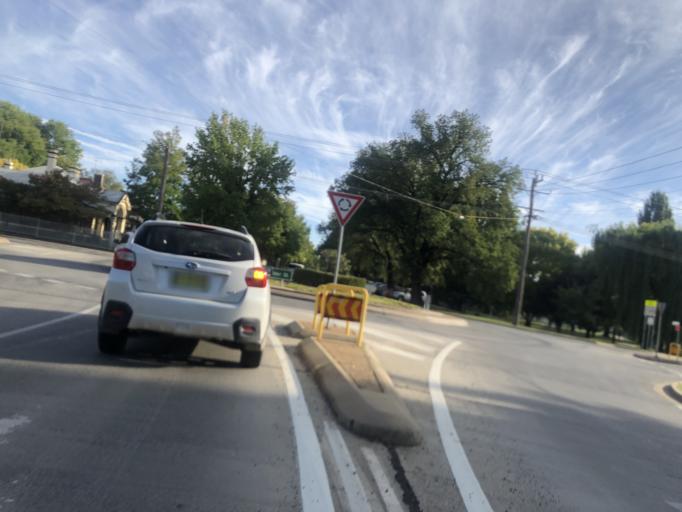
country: AU
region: New South Wales
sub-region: Orange Municipality
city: Orange
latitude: -33.2878
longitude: 149.0979
